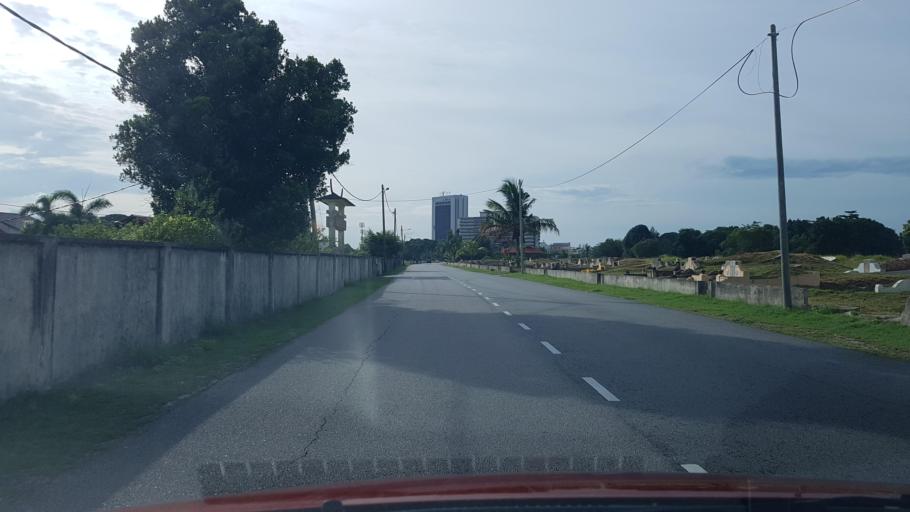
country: MY
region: Terengganu
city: Kuala Terengganu
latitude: 5.3226
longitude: 103.1456
